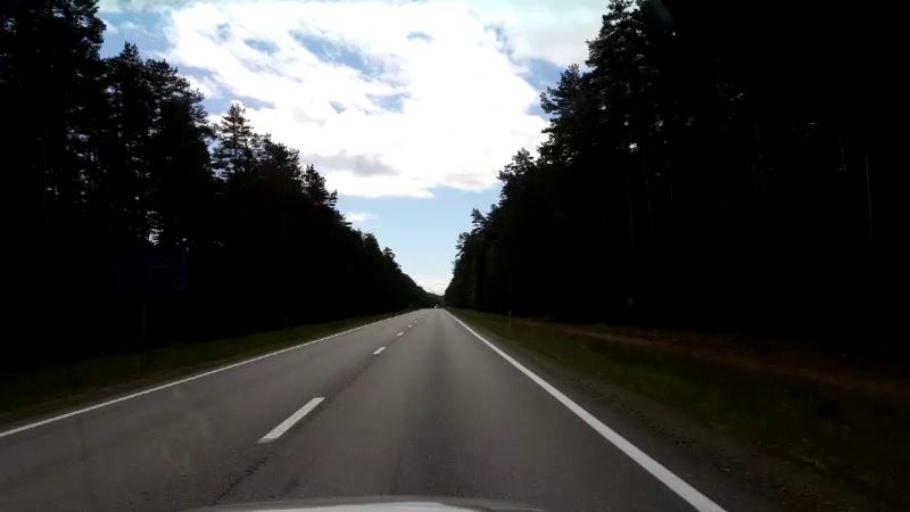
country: LV
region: Salacgrivas
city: Salacgriva
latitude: 57.5132
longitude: 24.4306
